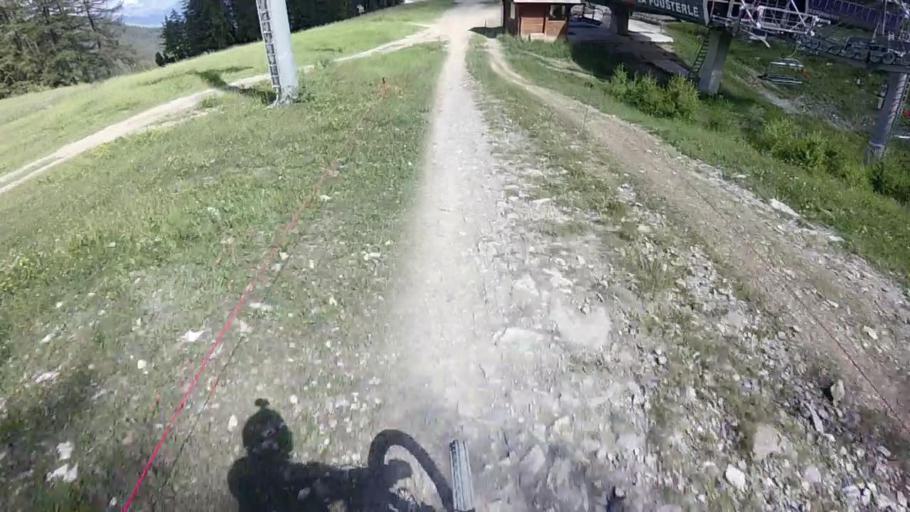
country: FR
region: Provence-Alpes-Cote d'Azur
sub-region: Departement des Hautes-Alpes
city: Embrun
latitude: 44.4823
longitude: 6.5615
